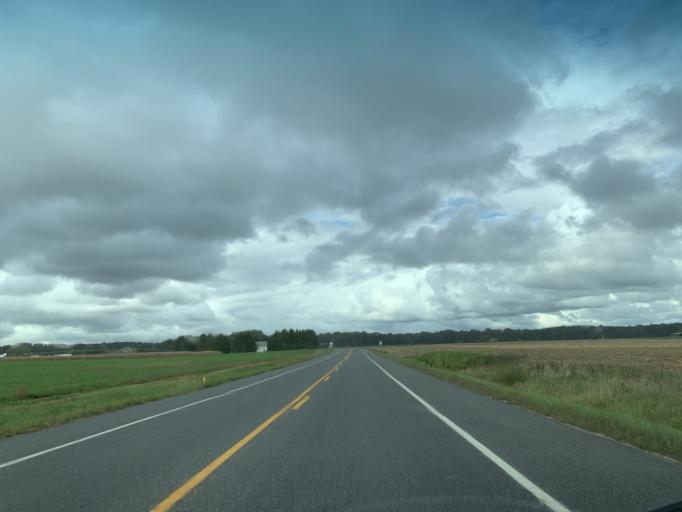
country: US
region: Maryland
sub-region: Caroline County
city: Ridgely
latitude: 39.0014
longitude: -75.8740
